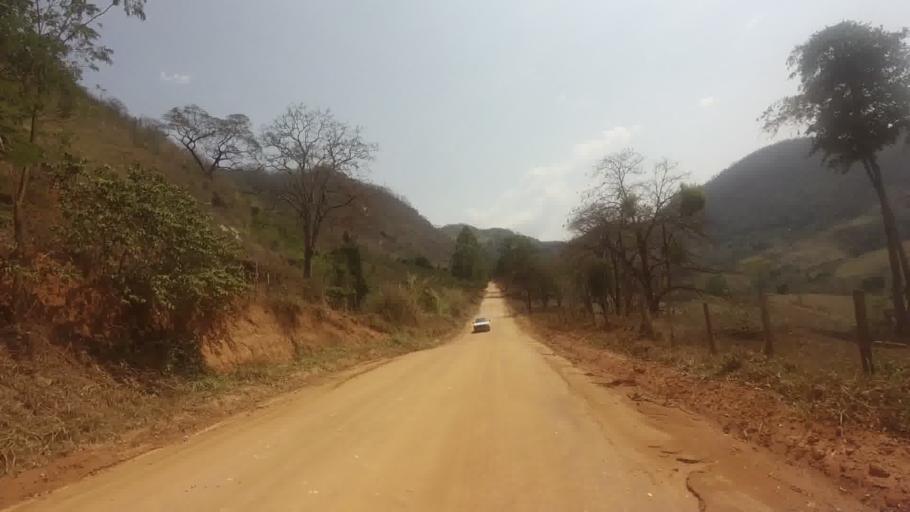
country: BR
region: Espirito Santo
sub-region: Mimoso Do Sul
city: Mimoso do Sul
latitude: -20.9478
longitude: -41.3854
